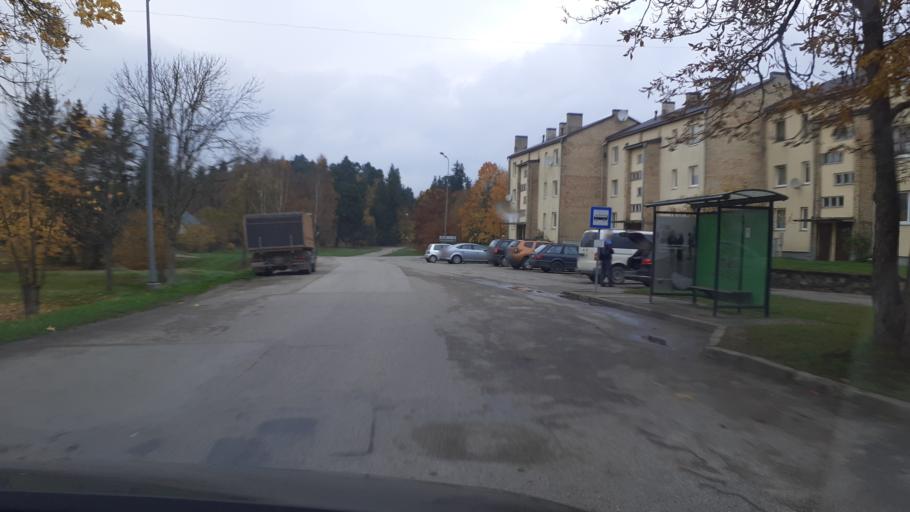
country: LV
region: Kuldigas Rajons
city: Kuldiga
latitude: 56.9850
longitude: 22.0190
